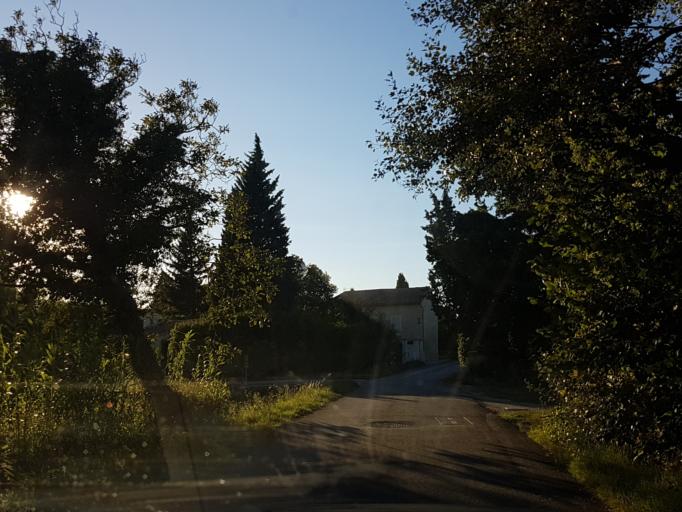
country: FR
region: Provence-Alpes-Cote d'Azur
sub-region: Departement du Vaucluse
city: Velleron
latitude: 43.9554
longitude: 5.0350
